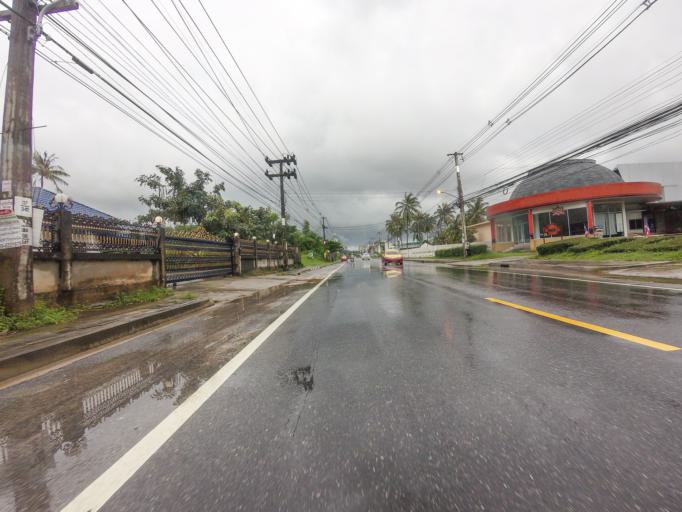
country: TH
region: Surat Thani
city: Ko Samui
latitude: 9.4566
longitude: 99.9922
